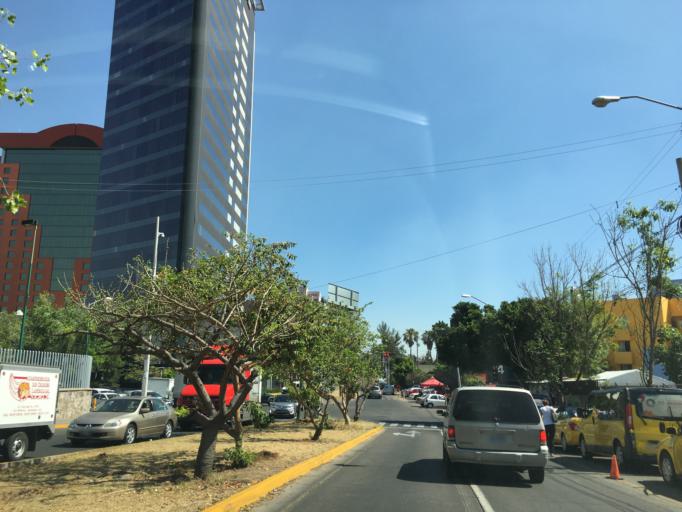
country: MX
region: Jalisco
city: Guadalajara
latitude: 20.6521
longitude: -103.3893
